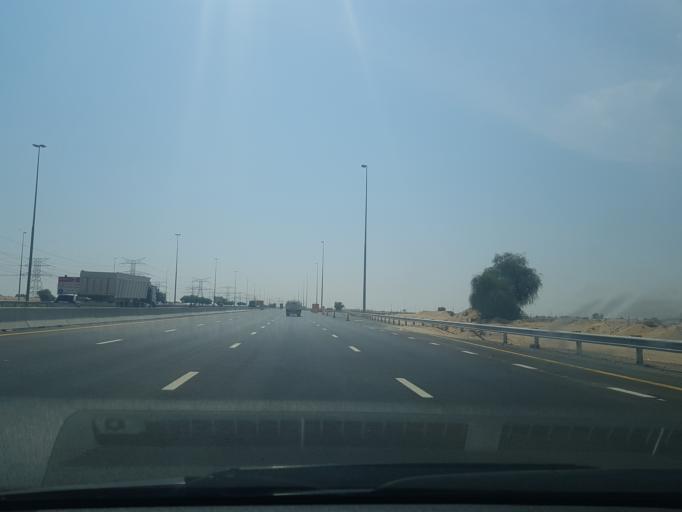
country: AE
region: Ash Shariqah
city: Sharjah
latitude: 25.2304
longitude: 55.5621
